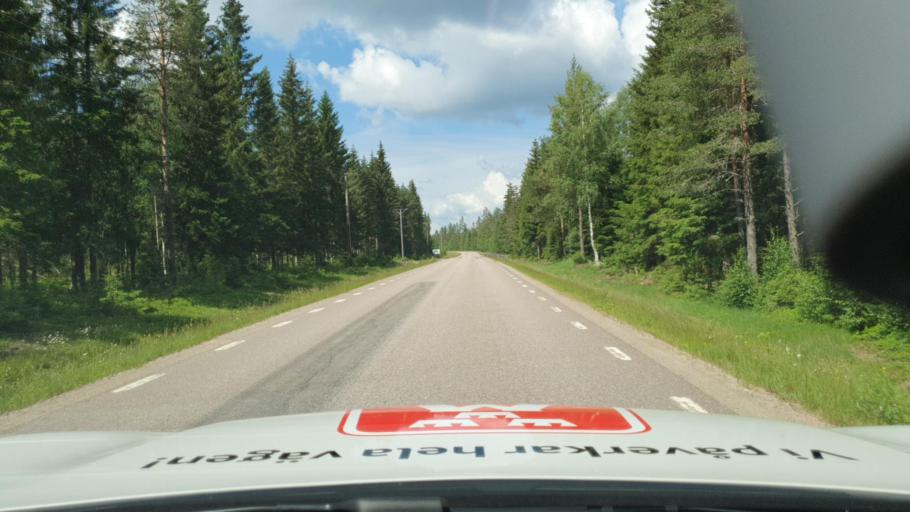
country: SE
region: Vaermland
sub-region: Torsby Kommun
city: Torsby
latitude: 60.4927
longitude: 12.8691
